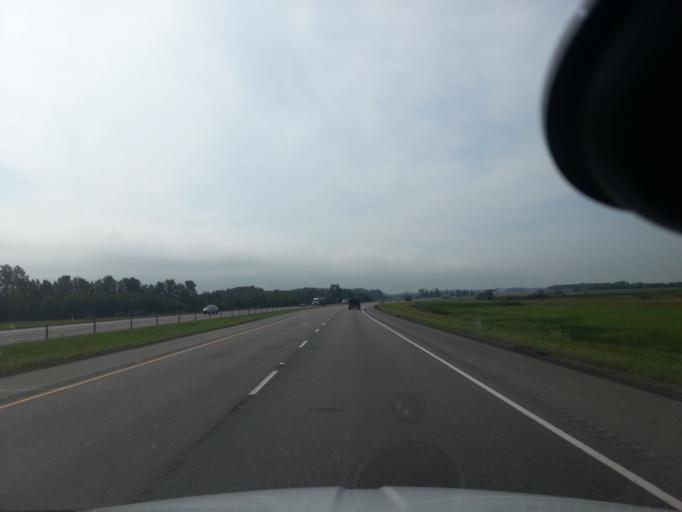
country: CA
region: Alberta
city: Penhold
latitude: 52.1835
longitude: -113.8164
